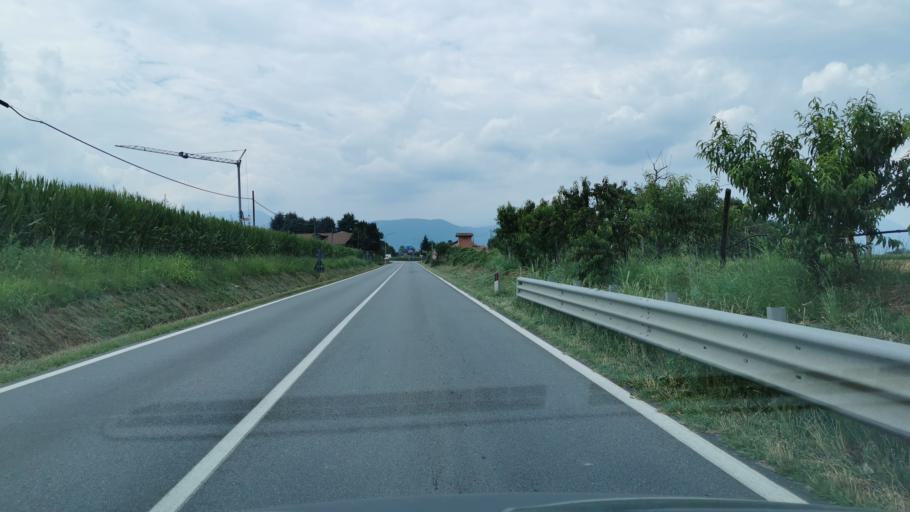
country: IT
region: Piedmont
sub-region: Provincia di Torino
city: Osasco
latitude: 44.8390
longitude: 7.3564
